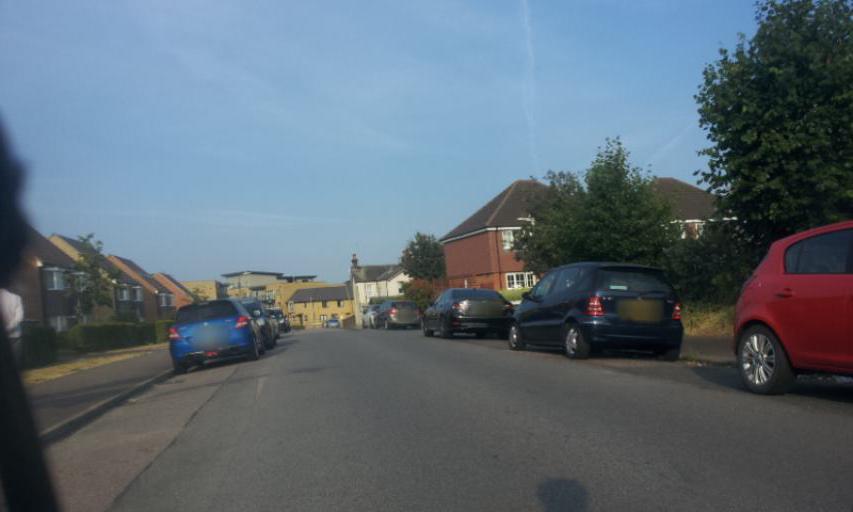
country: GB
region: England
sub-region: Kent
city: Dartford
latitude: 51.4538
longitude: 0.2097
